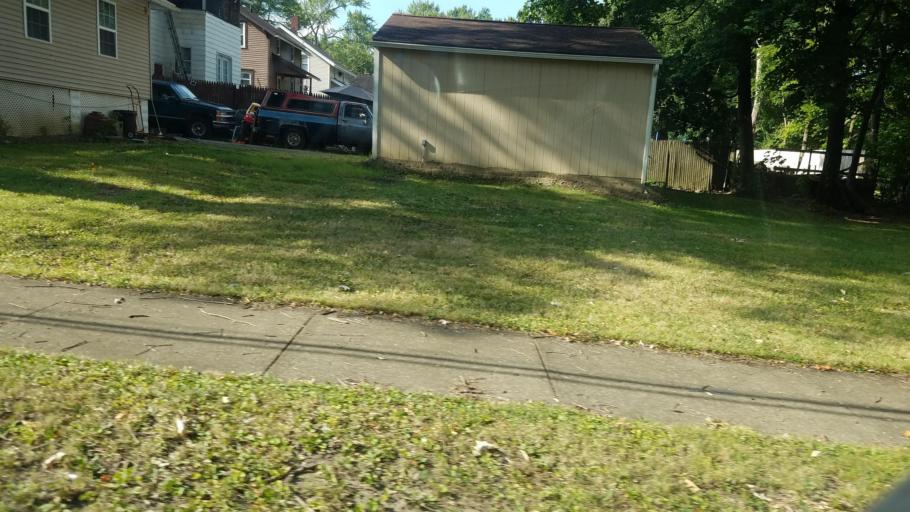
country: US
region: Ohio
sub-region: Mahoning County
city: Struthers
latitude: 41.0616
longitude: -80.6072
